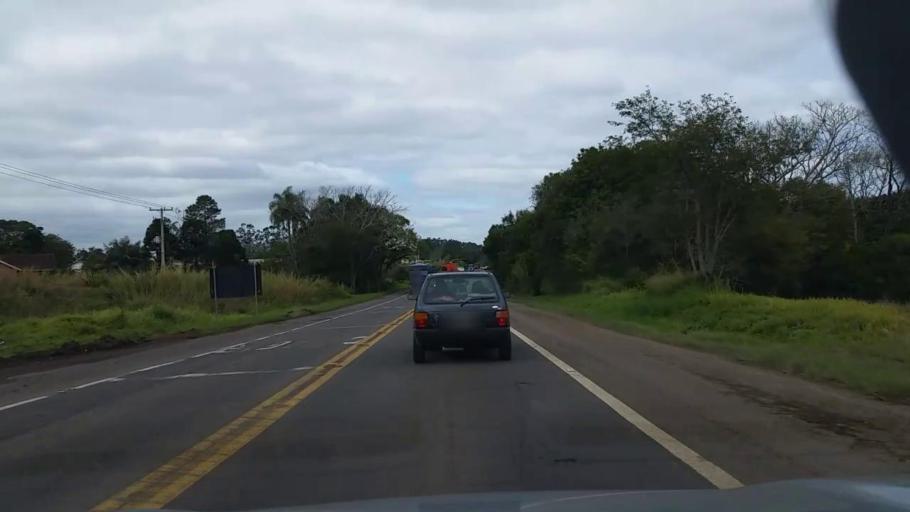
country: BR
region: Rio Grande do Sul
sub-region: Arroio Do Meio
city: Arroio do Meio
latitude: -29.4048
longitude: -52.0356
